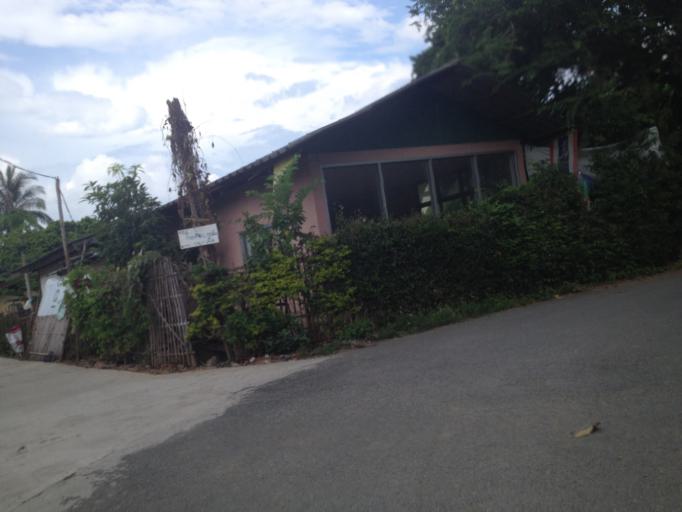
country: TH
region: Chiang Mai
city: Hang Dong
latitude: 18.7135
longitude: 98.9294
